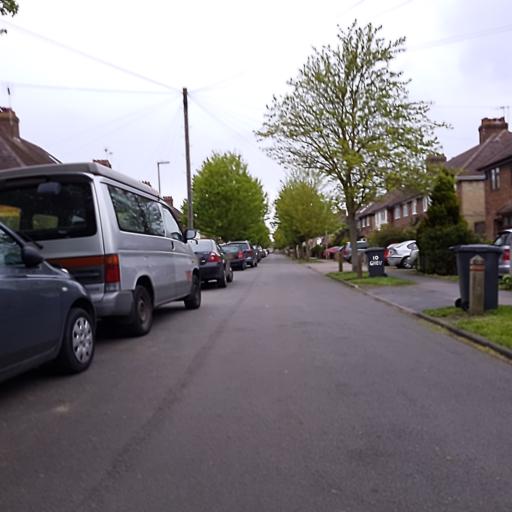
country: GB
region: England
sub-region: Cambridgeshire
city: Cambridge
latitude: 52.1954
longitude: 0.1465
